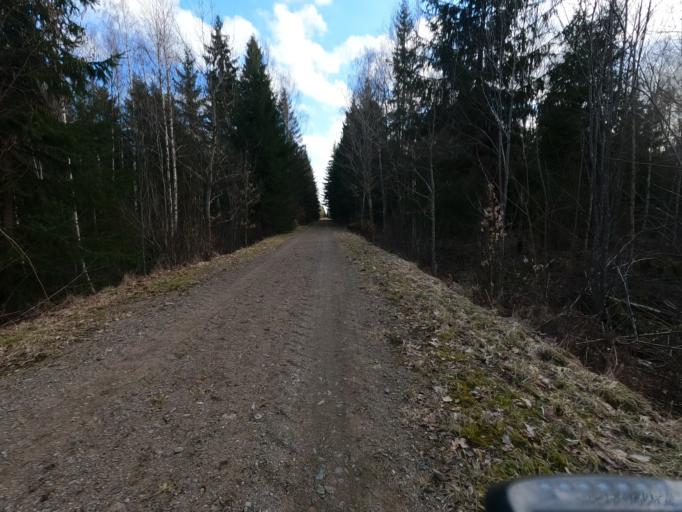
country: SE
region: Kronoberg
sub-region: Alvesta Kommun
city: Vislanda
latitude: 56.6528
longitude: 14.6181
